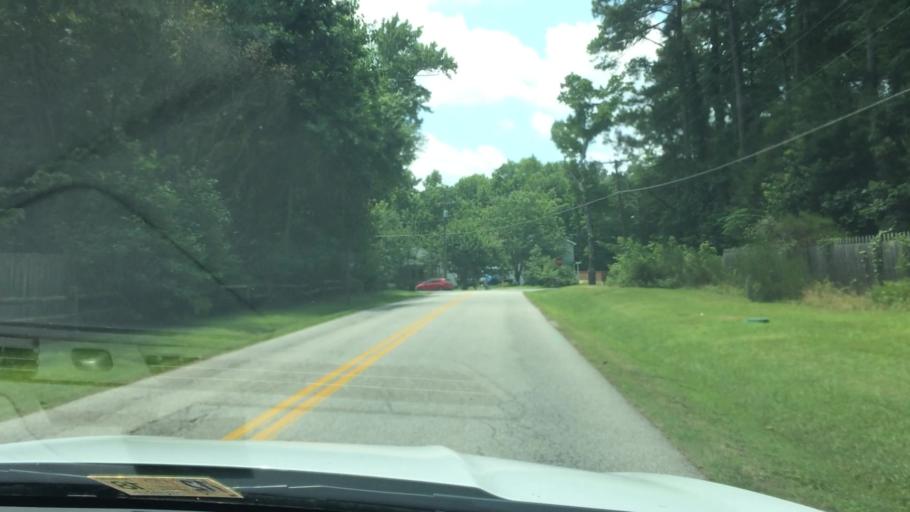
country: US
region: Virginia
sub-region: York County
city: Yorktown
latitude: 37.2011
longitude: -76.4859
